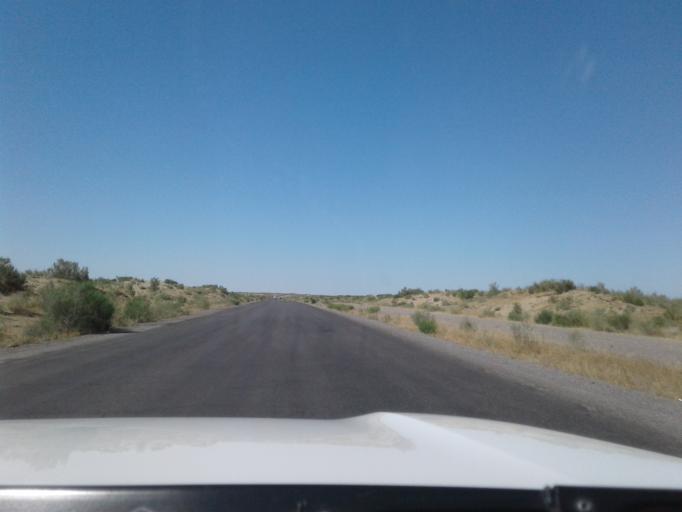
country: TM
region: Mary
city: Bayramaly
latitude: 38.1367
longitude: 62.8310
